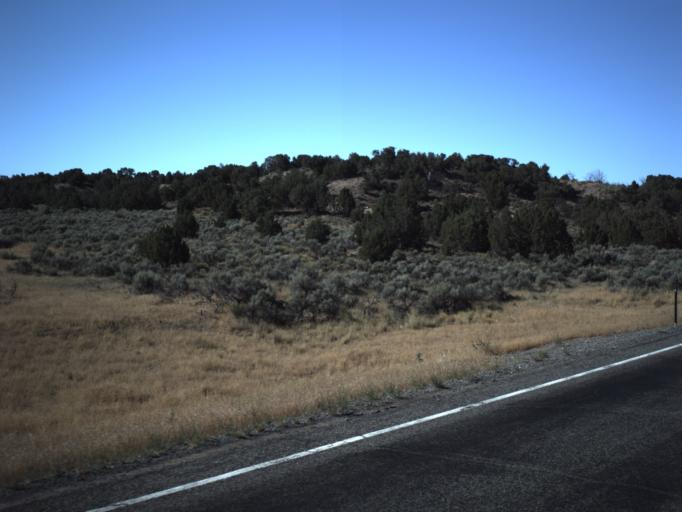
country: US
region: Utah
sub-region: Juab County
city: Mona
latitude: 39.7625
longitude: -112.1745
